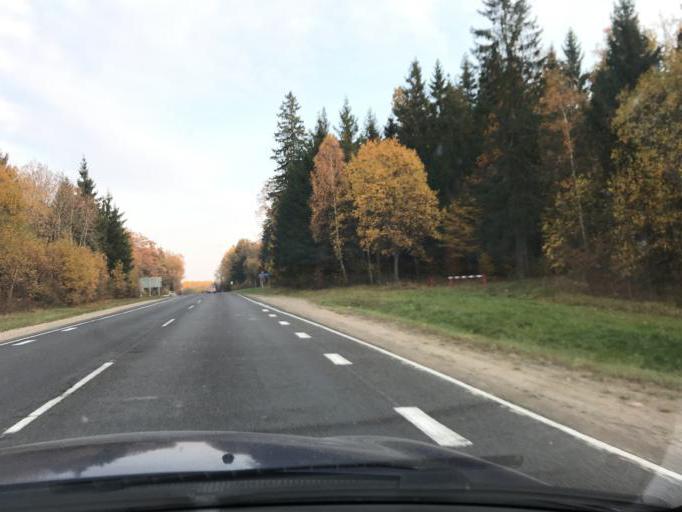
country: BY
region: Grodnenskaya
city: Navahrudak
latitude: 53.5890
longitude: 25.8909
